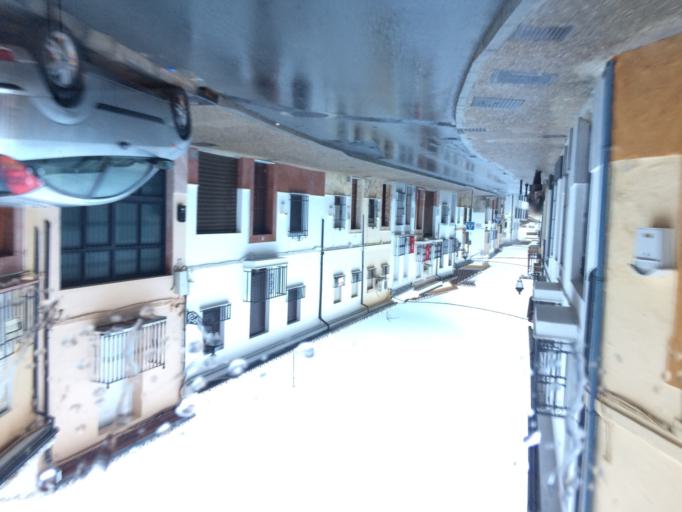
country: ES
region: Andalusia
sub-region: Provincia de Malaga
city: Antequera
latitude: 37.0225
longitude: -4.5579
